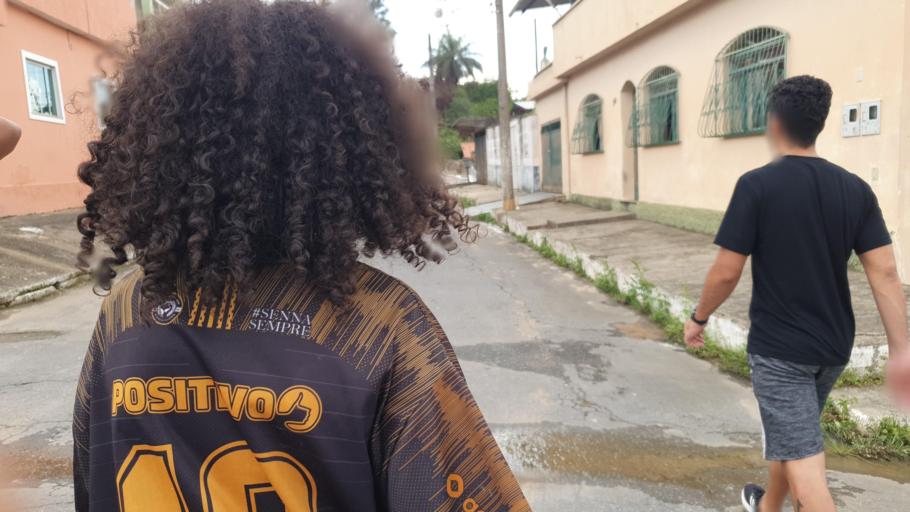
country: BR
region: Minas Gerais
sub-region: Sao Joao Del Rei
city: Sao Joao del Rei
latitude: -21.1273
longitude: -44.2631
